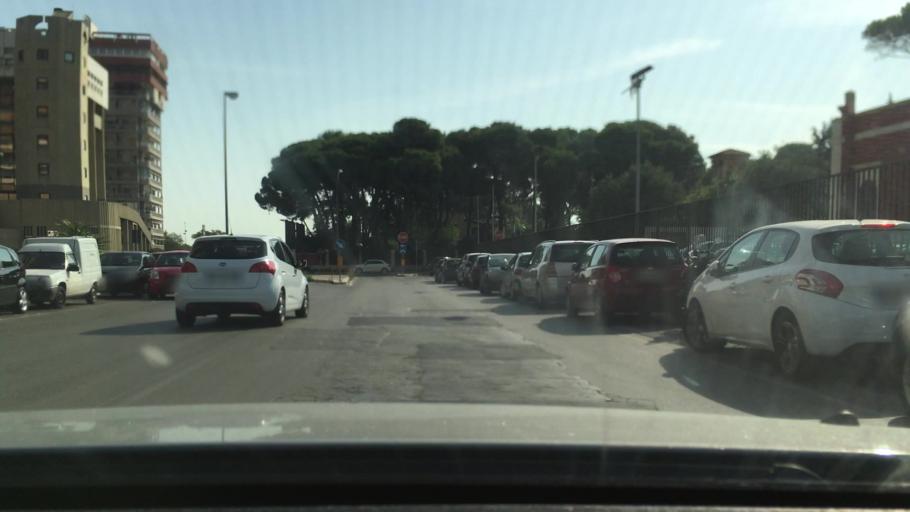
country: IT
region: Apulia
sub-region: Provincia di Bari
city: Bari
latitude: 41.1001
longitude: 16.8877
